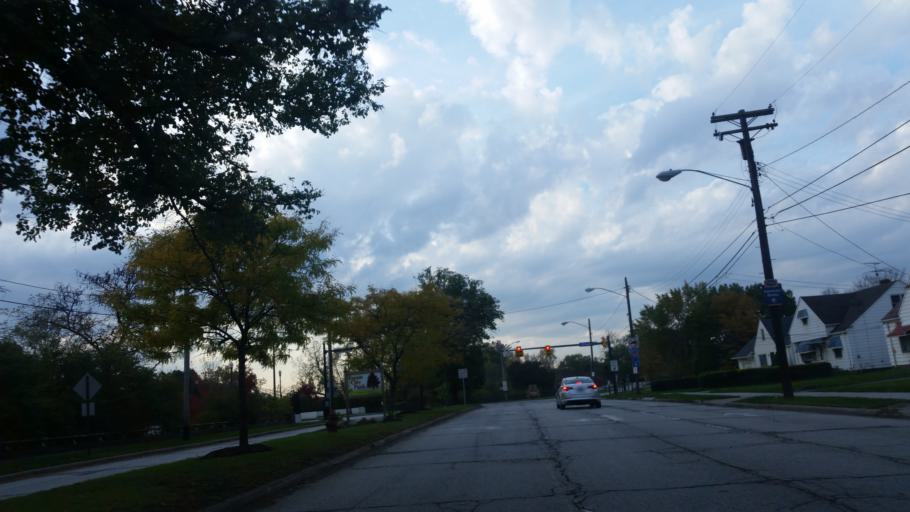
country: US
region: Ohio
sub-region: Cuyahoga County
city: Newburgh Heights
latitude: 41.4567
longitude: -81.6578
